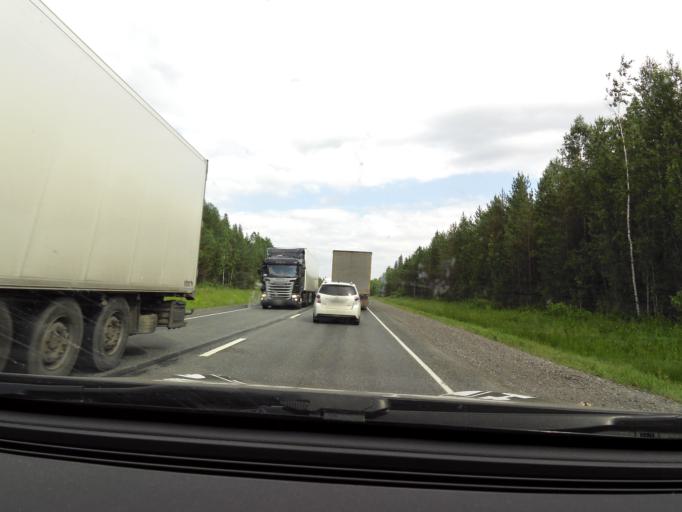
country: RU
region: Sverdlovsk
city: Nizhniye Sergi
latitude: 56.8245
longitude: 59.2803
